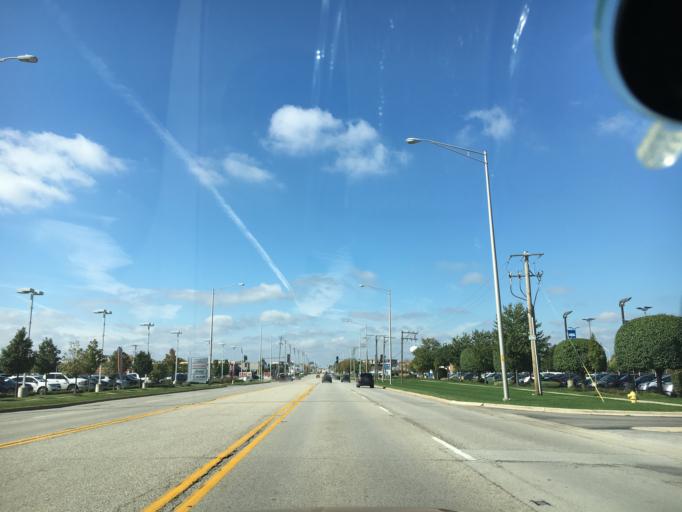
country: US
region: Illinois
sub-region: Cook County
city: Orland Hills
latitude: 41.6019
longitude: -87.8211
